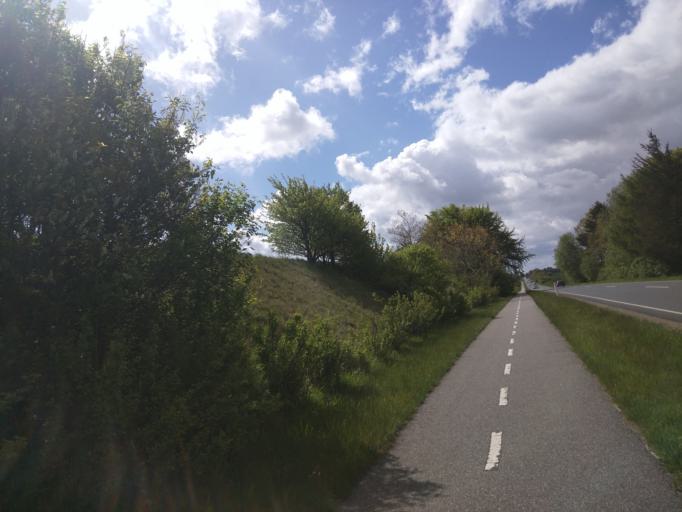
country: DK
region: Central Jutland
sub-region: Silkeborg Kommune
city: Kjellerup
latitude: 56.3178
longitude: 9.4205
